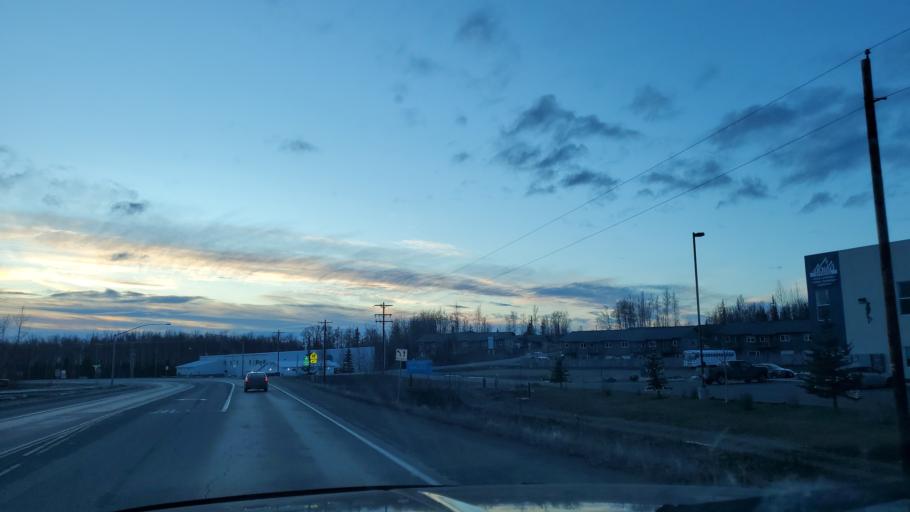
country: US
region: Alaska
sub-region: Matanuska-Susitna Borough
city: Wasilla
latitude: 61.5904
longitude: -149.4411
